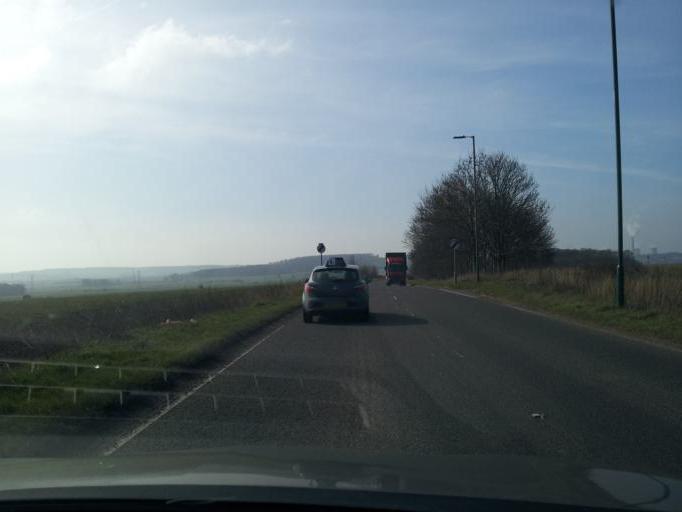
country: GB
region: England
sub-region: Nottinghamshire
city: Gotham
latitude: 52.8937
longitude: -1.1935
